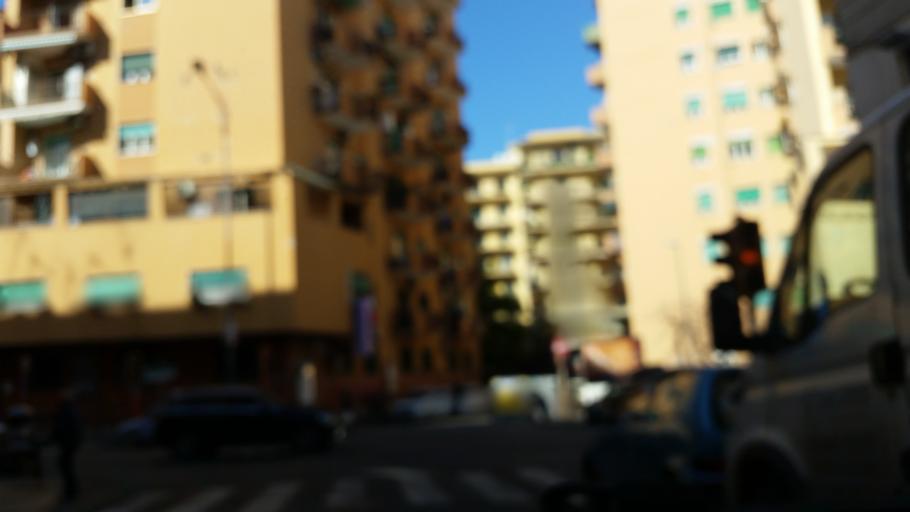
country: IT
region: Campania
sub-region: Provincia di Napoli
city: Napoli
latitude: 40.8429
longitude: 14.2217
